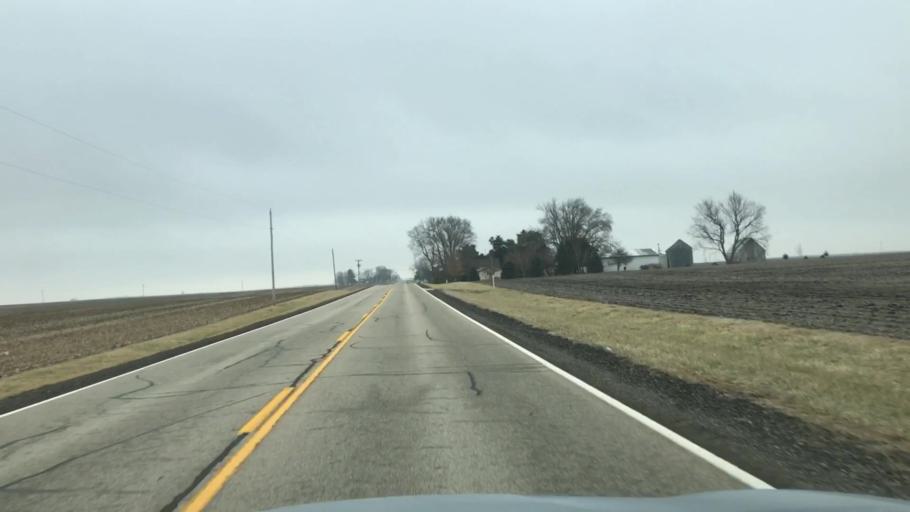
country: US
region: Illinois
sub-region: McLean County
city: Hudson
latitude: 40.6119
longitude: -88.9454
